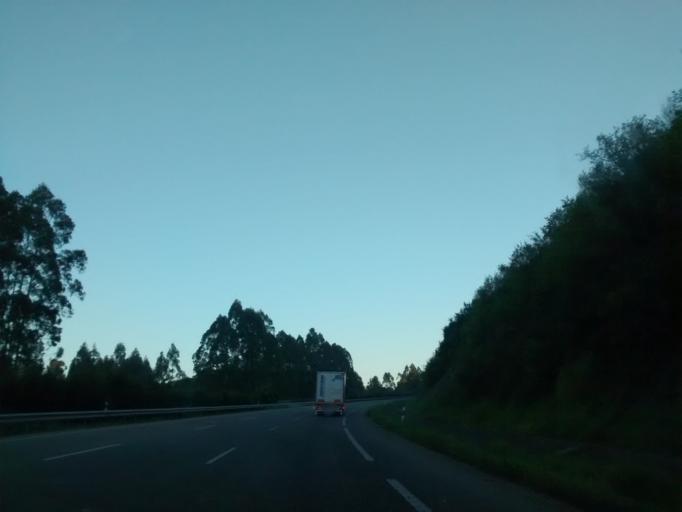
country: ES
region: Asturias
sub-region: Province of Asturias
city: Colunga
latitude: 43.4966
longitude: -5.3281
